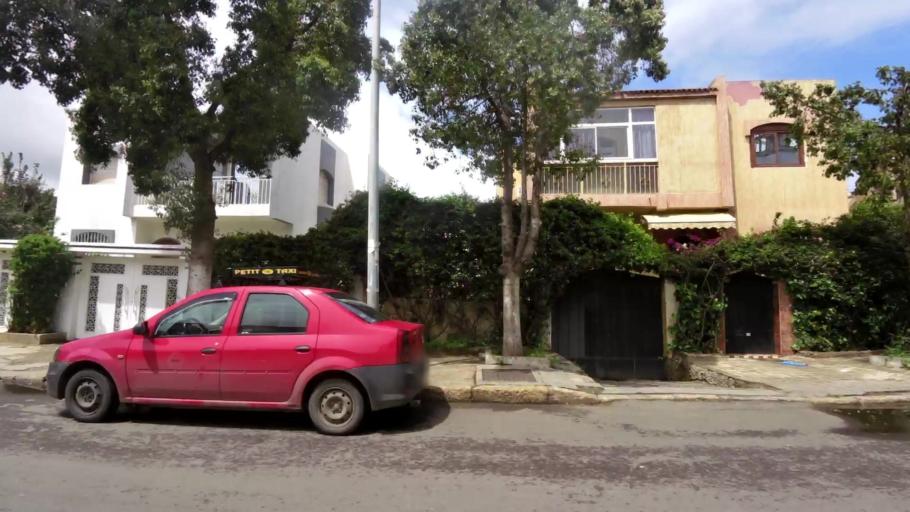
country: MA
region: Grand Casablanca
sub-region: Casablanca
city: Casablanca
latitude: 33.5456
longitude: -7.6828
